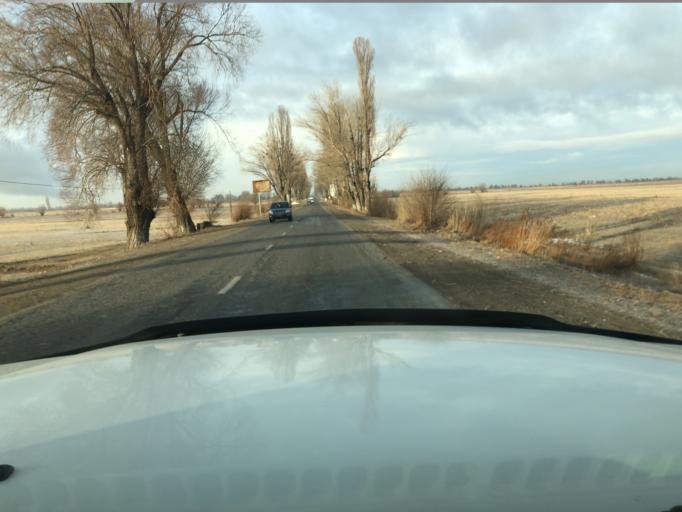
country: KG
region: Ysyk-Koel
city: Karakol
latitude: 42.4754
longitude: 78.3111
